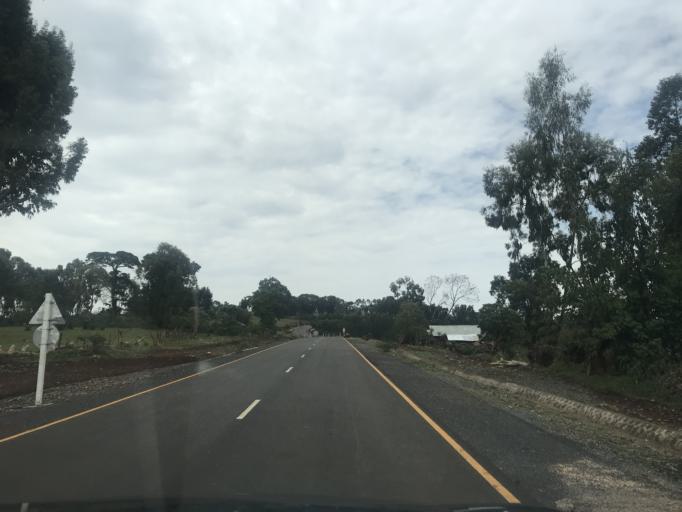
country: ET
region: Oromiya
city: Shambu
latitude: 9.8855
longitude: 36.6665
